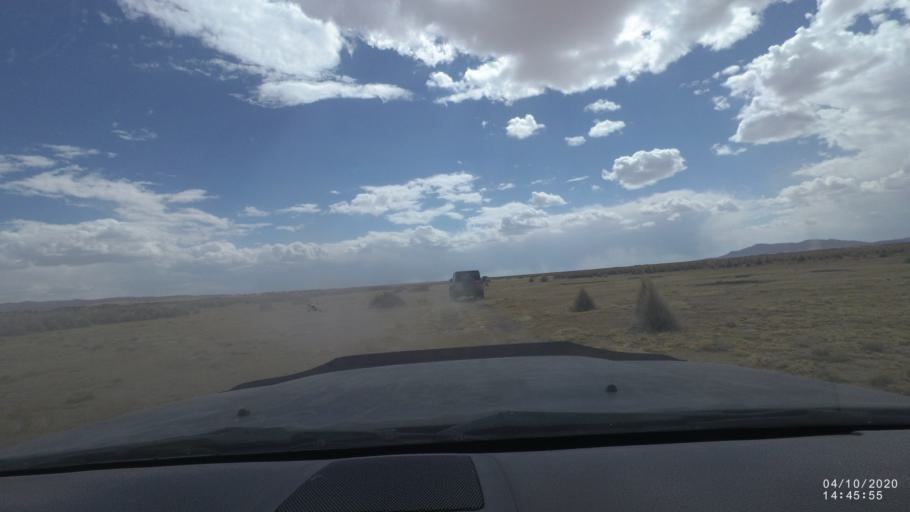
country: BO
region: Oruro
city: Poopo
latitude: -18.6865
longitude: -67.5002
